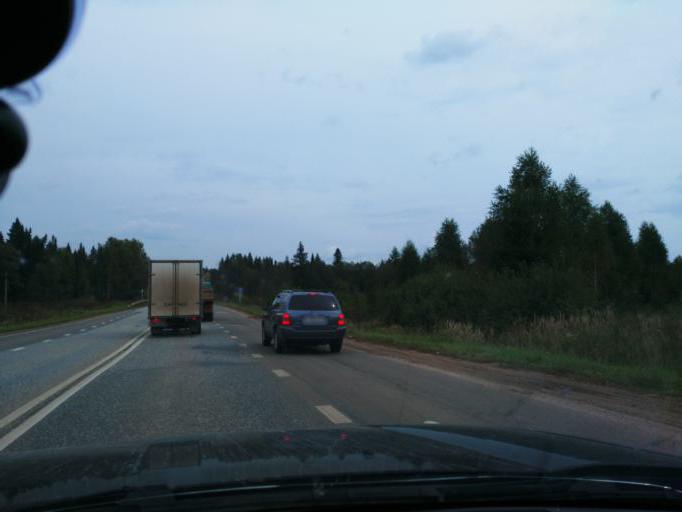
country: RU
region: Perm
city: Chernushka
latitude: 56.5019
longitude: 55.8672
